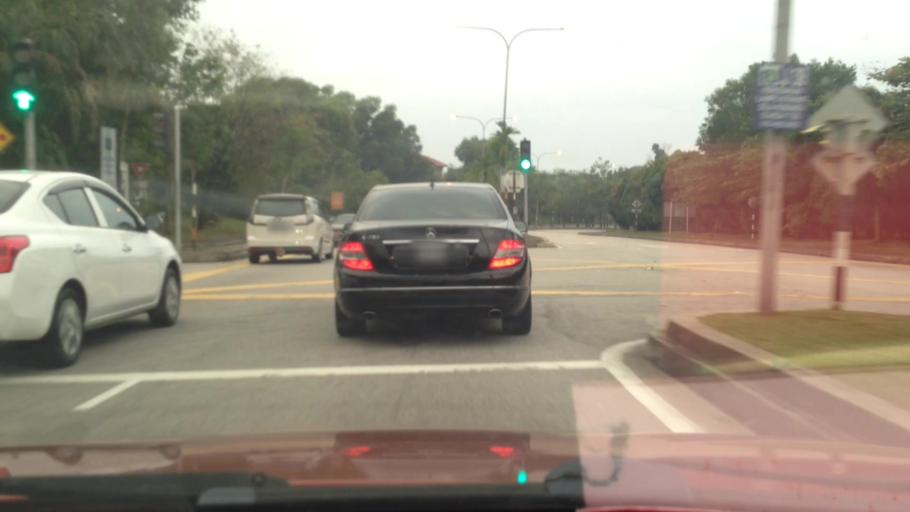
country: MY
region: Selangor
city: Subang Jaya
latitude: 3.0599
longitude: 101.5704
